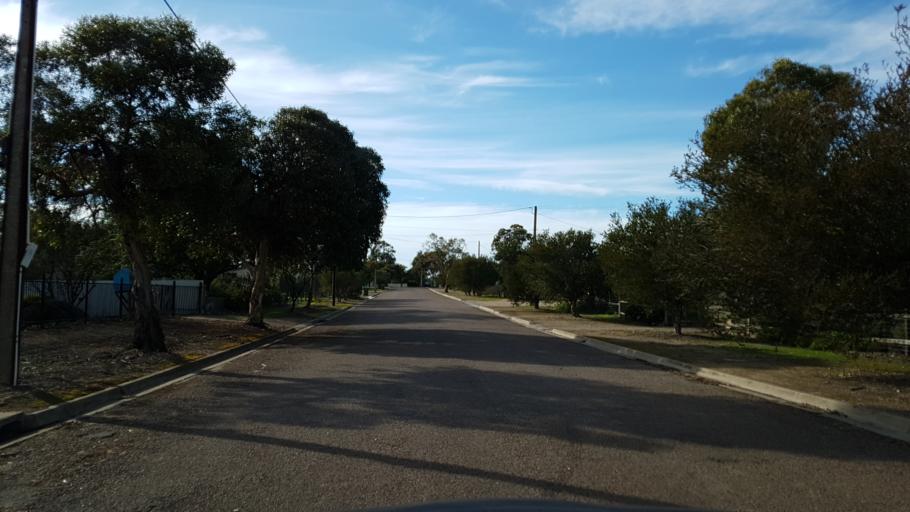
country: AU
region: South Australia
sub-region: Murray Bridge
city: Tailem Bend
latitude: -35.2527
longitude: 139.4603
